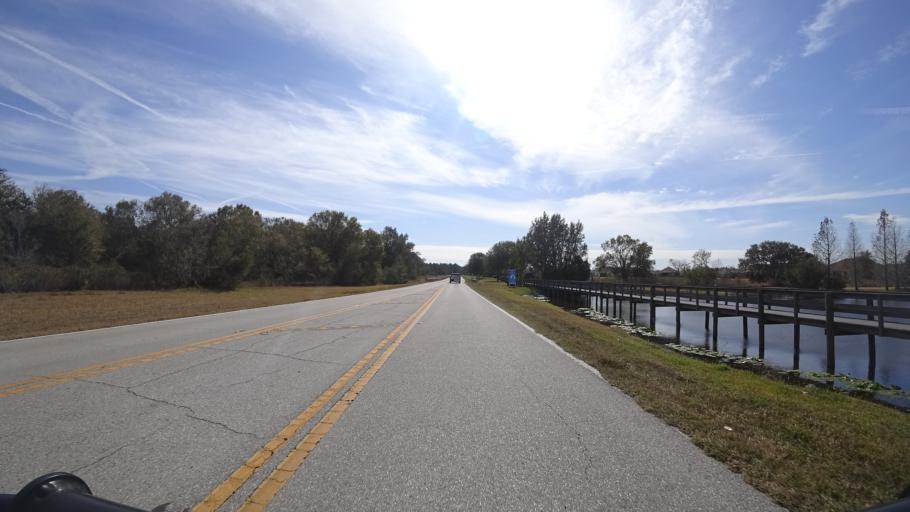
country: US
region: Florida
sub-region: Manatee County
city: Ellenton
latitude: 27.5240
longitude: -82.3673
